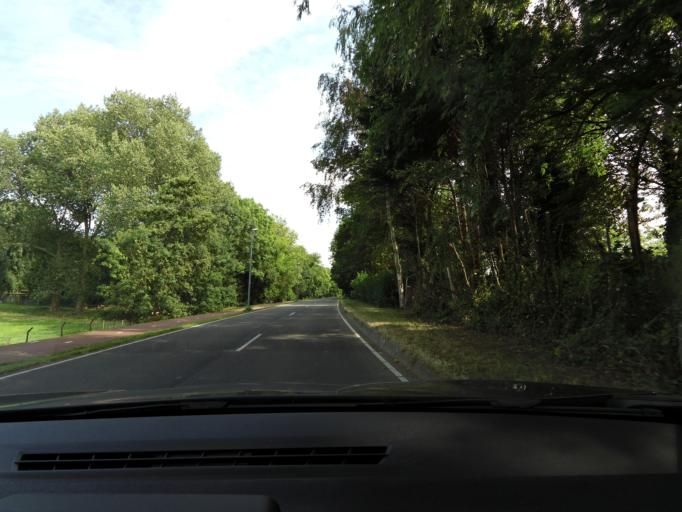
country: NL
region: South Holland
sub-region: Gemeente Schiedam
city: Schiedam
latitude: 51.9542
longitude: 4.4040
